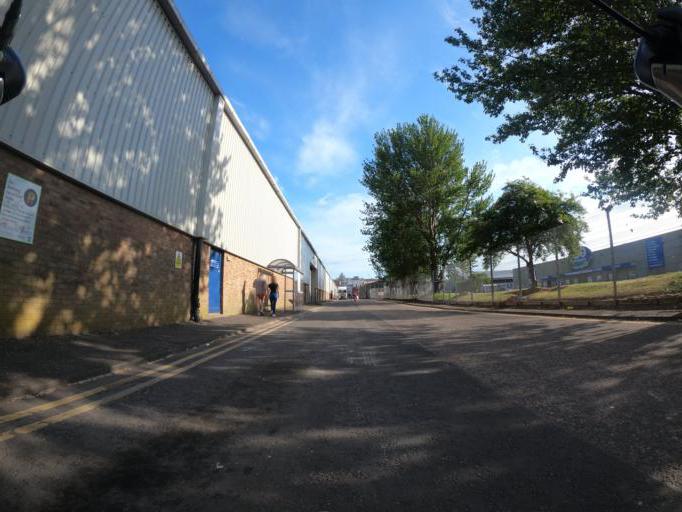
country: GB
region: Scotland
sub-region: Edinburgh
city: Edinburgh
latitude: 55.9831
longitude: -3.2251
